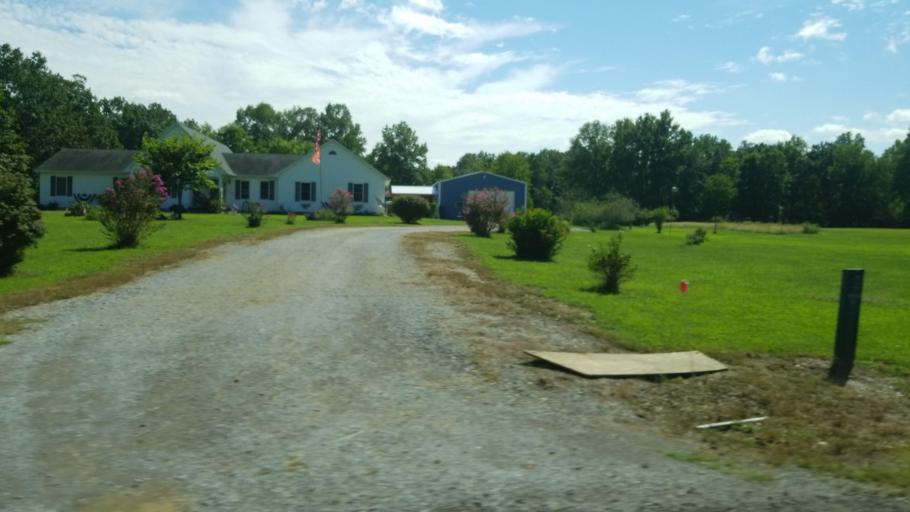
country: US
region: Illinois
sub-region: Williamson County
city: Johnston City
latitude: 37.7895
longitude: -88.8873
